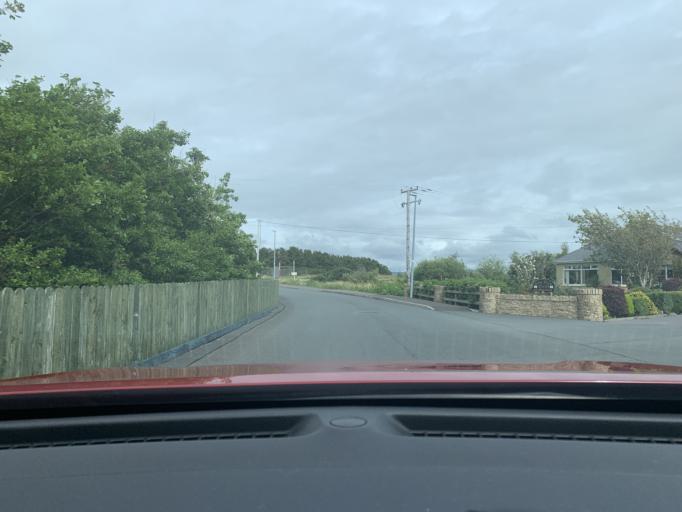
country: IE
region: Ulster
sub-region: County Donegal
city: Dungloe
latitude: 54.9534
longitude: -8.3701
